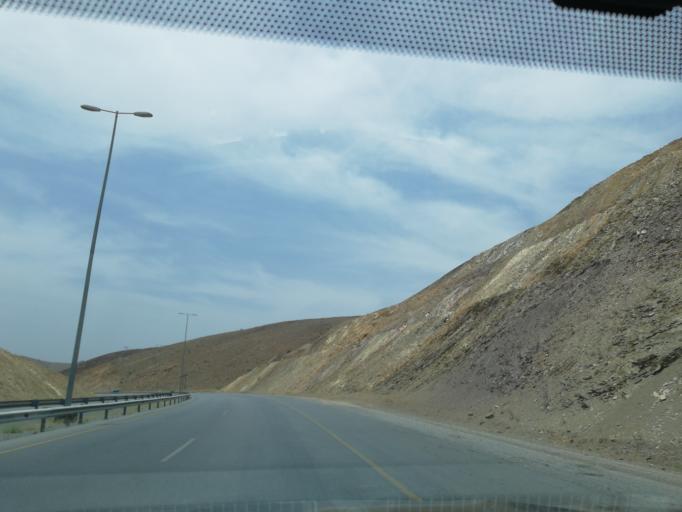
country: OM
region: Muhafazat ad Dakhiliyah
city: Izki
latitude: 22.8959
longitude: 57.7179
